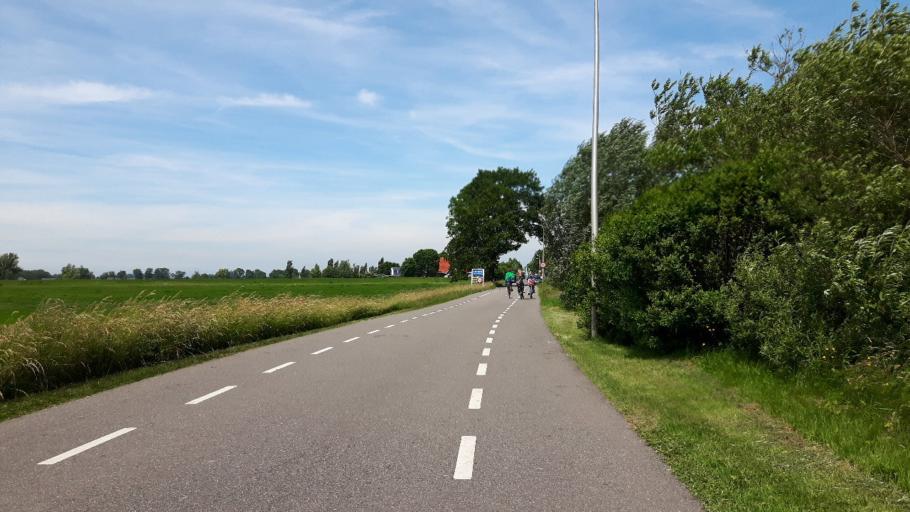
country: NL
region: South Holland
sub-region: Gemeente Nieuwkoop
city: Nieuwkoop
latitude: 52.1579
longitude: 4.7262
